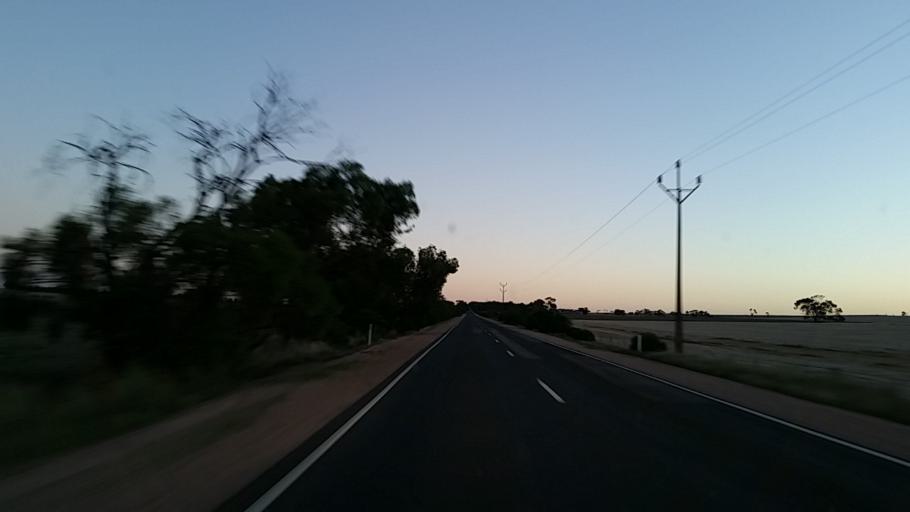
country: AU
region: South Australia
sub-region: Clare and Gilbert Valleys
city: Clare
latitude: -33.9716
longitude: 138.5013
